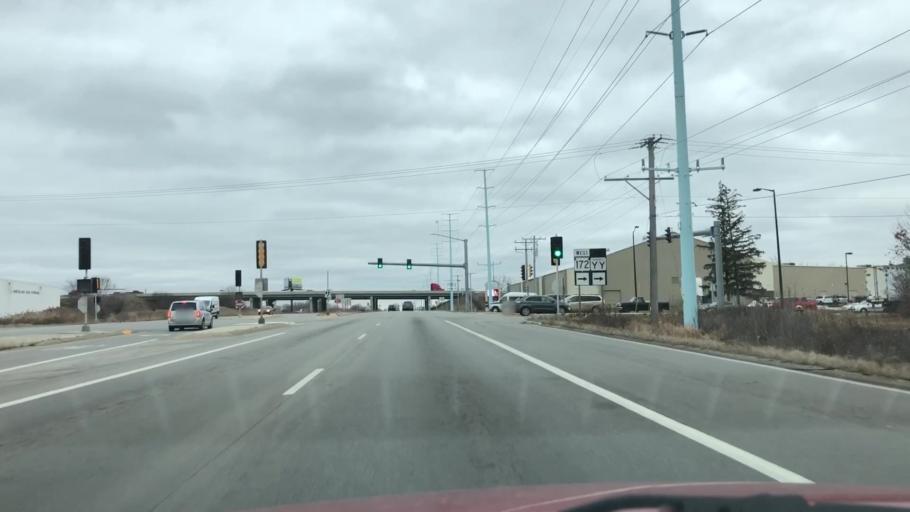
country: US
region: Wisconsin
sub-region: Brown County
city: Ashwaubenon
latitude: 44.4808
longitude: -88.0577
